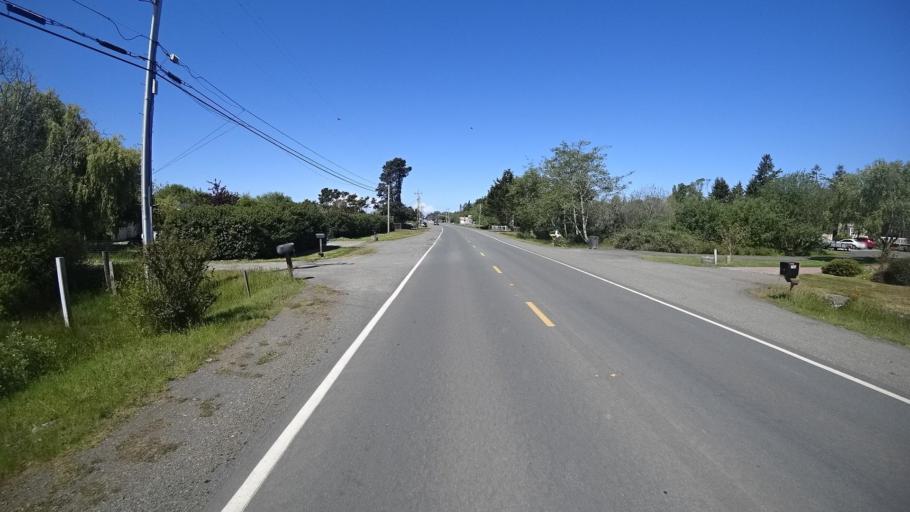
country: US
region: California
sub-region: Humboldt County
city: McKinleyville
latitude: 40.9561
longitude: -124.0972
